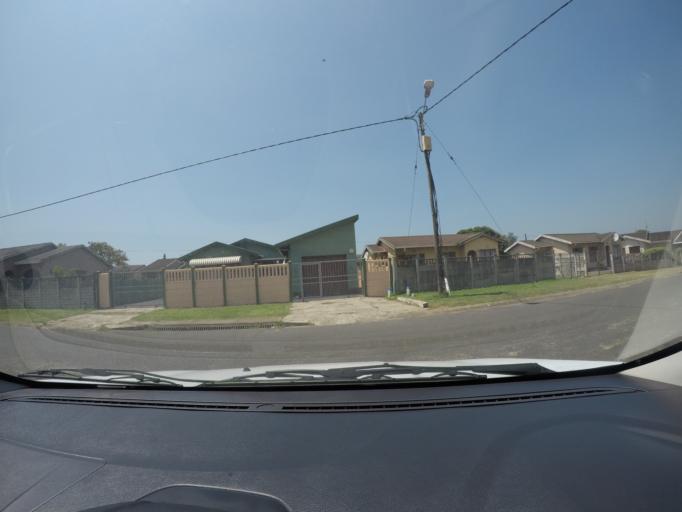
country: ZA
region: KwaZulu-Natal
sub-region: uThungulu District Municipality
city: eSikhawini
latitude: -28.8693
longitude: 31.9208
